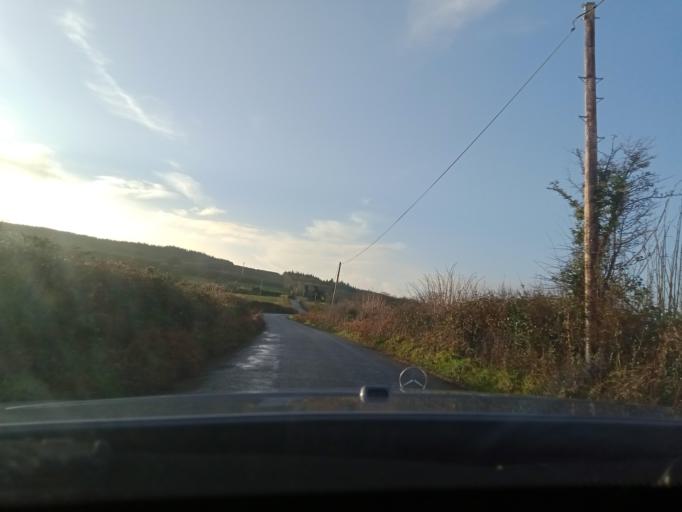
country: IE
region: Leinster
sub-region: Kilkenny
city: Callan
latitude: 52.4773
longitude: -7.4304
